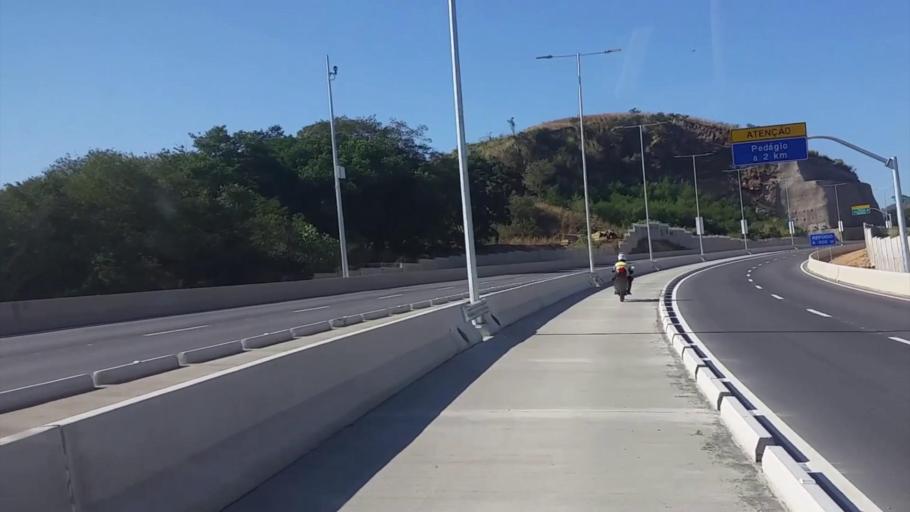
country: BR
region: Rio de Janeiro
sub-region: Nilopolis
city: Nilopolis
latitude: -22.8785
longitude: -43.4017
